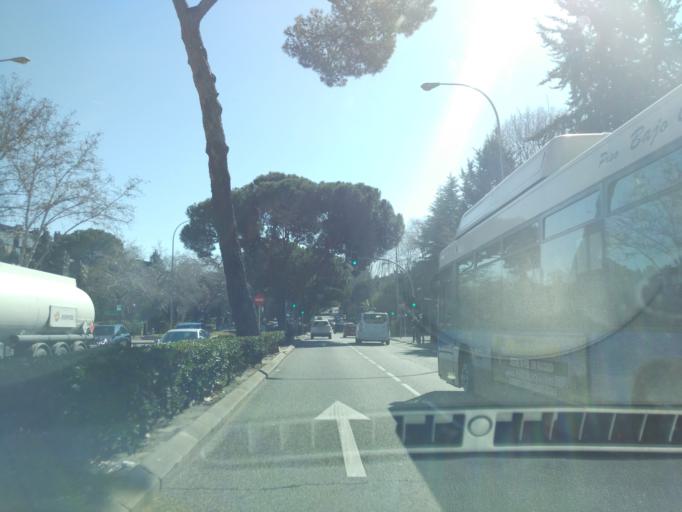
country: ES
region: Madrid
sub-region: Provincia de Madrid
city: Ciudad Lineal
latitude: 40.4546
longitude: -3.6554
